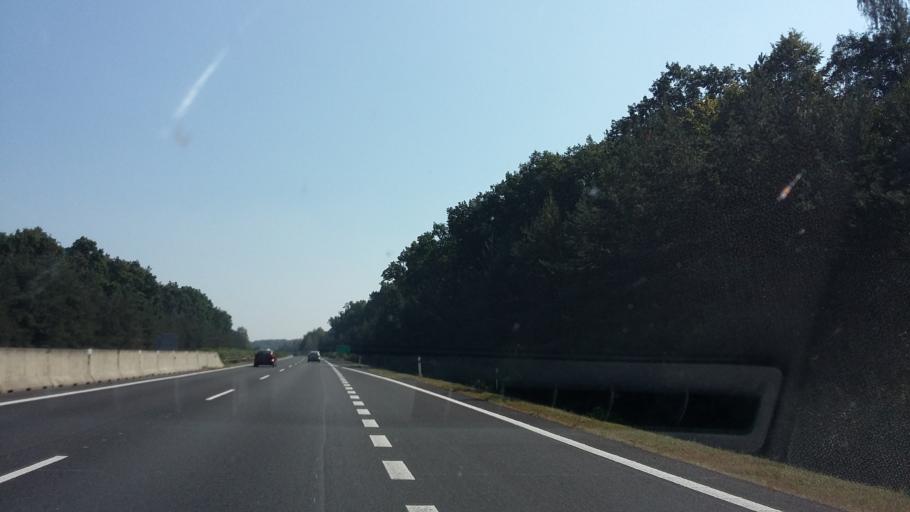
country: CZ
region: Central Bohemia
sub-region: Okres Nymburk
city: Podebrady
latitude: 50.1177
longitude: 15.1282
